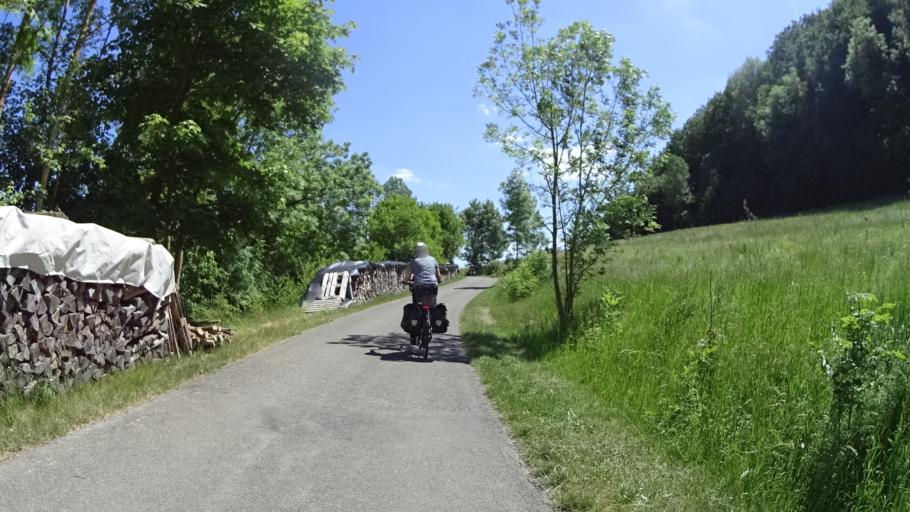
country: DE
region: Bavaria
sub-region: Regierungsbezirk Mittelfranken
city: Adelshofen
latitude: 49.4460
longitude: 10.1154
